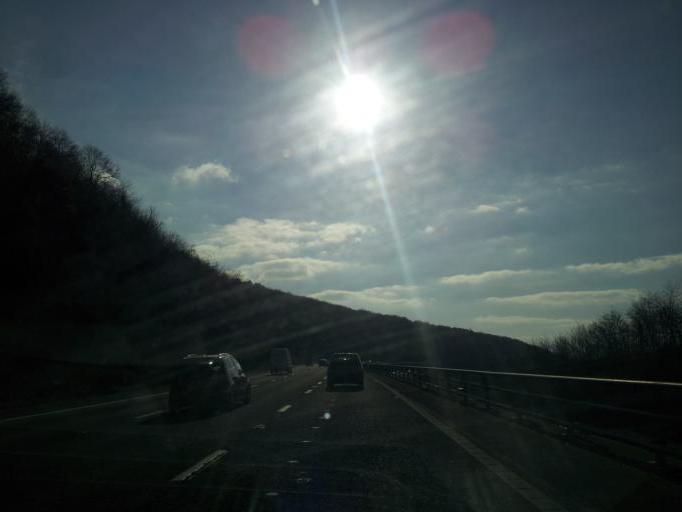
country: GB
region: England
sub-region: North Somerset
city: Portishead
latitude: 51.4565
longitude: -2.7691
